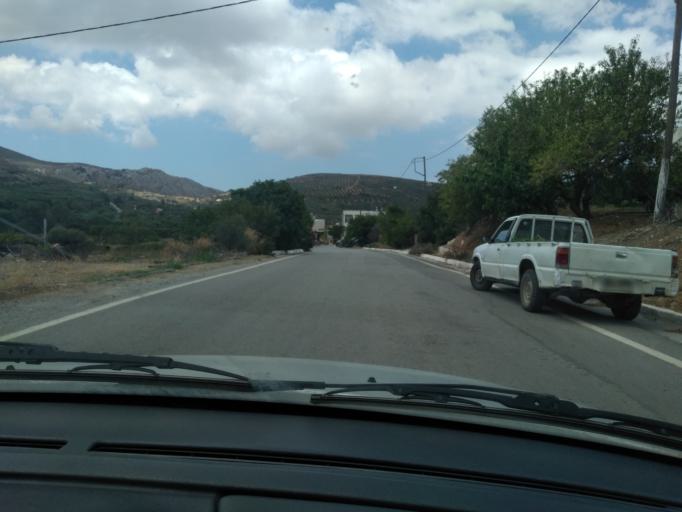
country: GR
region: Crete
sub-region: Nomos Lasithiou
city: Makry-Gialos
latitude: 35.0746
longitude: 26.0474
